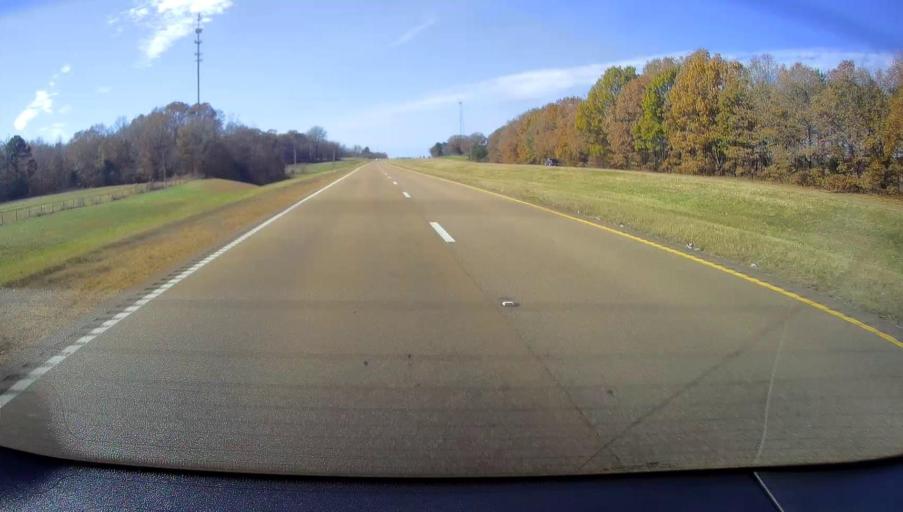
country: US
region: Mississippi
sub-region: Benton County
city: Ashland
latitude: 34.9461
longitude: -89.1360
